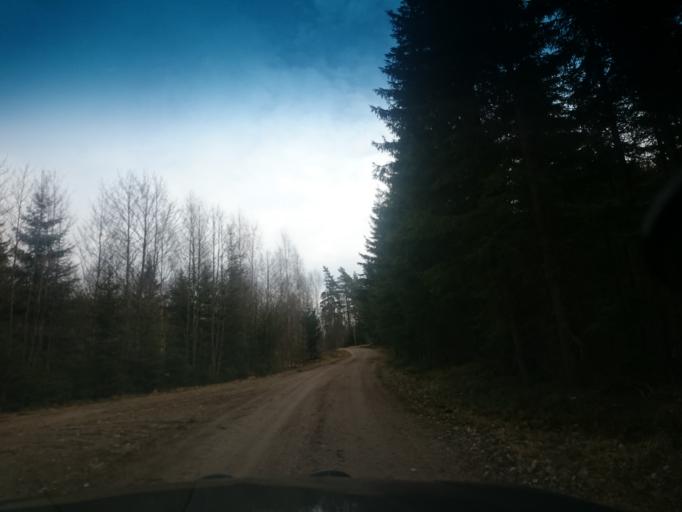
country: SE
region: Joenkoeping
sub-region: Vetlanda Kommun
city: Vetlanda
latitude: 57.3251
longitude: 15.1749
